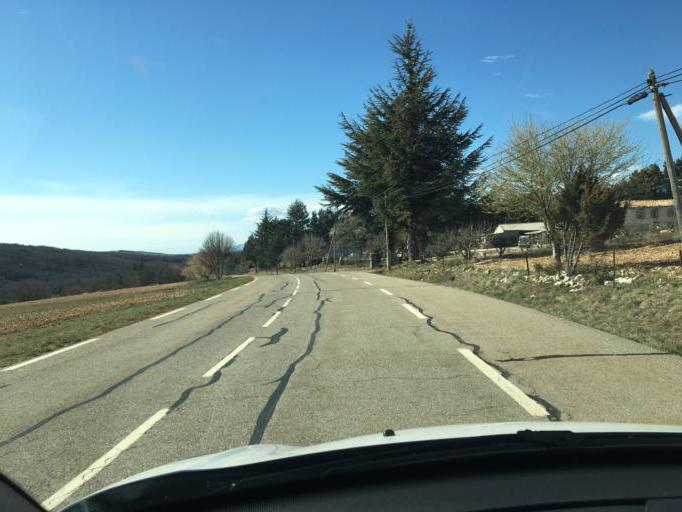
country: FR
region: Provence-Alpes-Cote d'Azur
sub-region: Departement du Vaucluse
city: Sault
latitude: 44.0050
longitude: 5.4821
